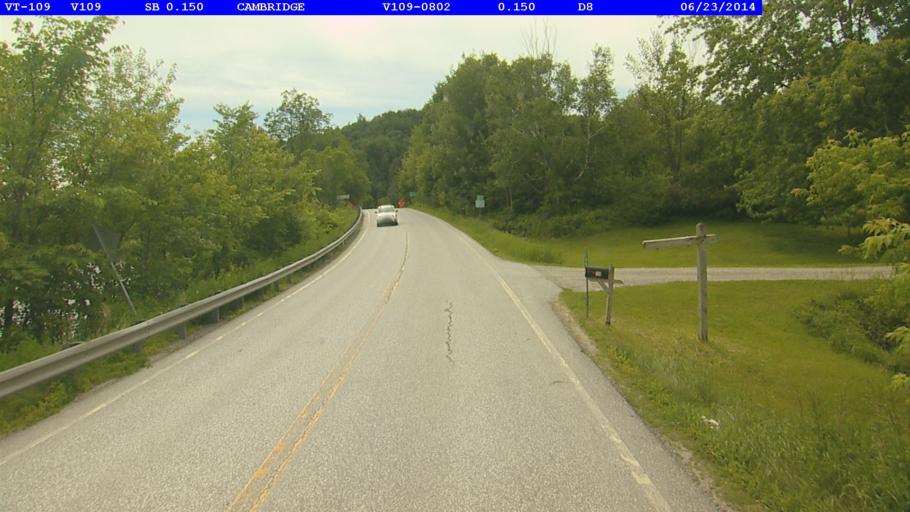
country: US
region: Vermont
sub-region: Lamoille County
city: Johnson
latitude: 44.6537
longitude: -72.8251
